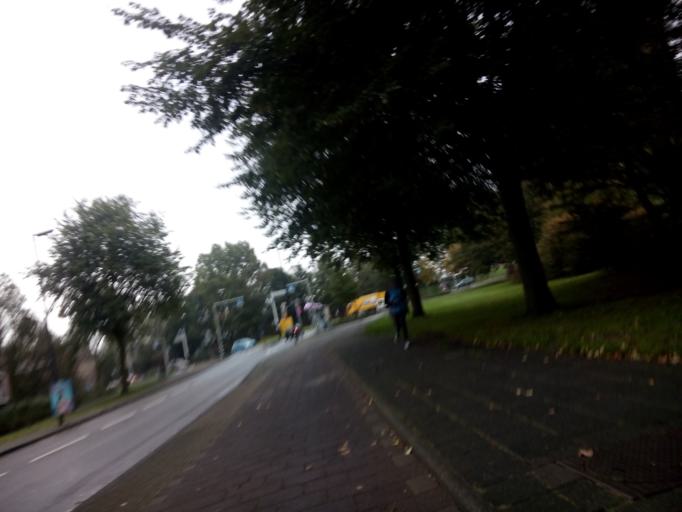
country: NL
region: South Holland
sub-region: Gemeente Maassluis
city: Maassluis
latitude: 51.9259
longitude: 4.2513
